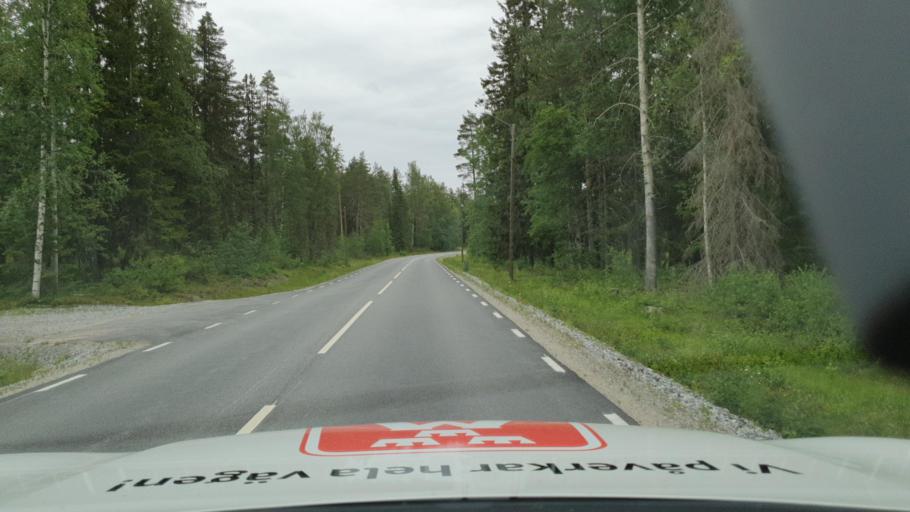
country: SE
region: Vaesterbotten
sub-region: Nordmalings Kommun
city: Nordmaling
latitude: 63.5051
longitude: 19.3303
